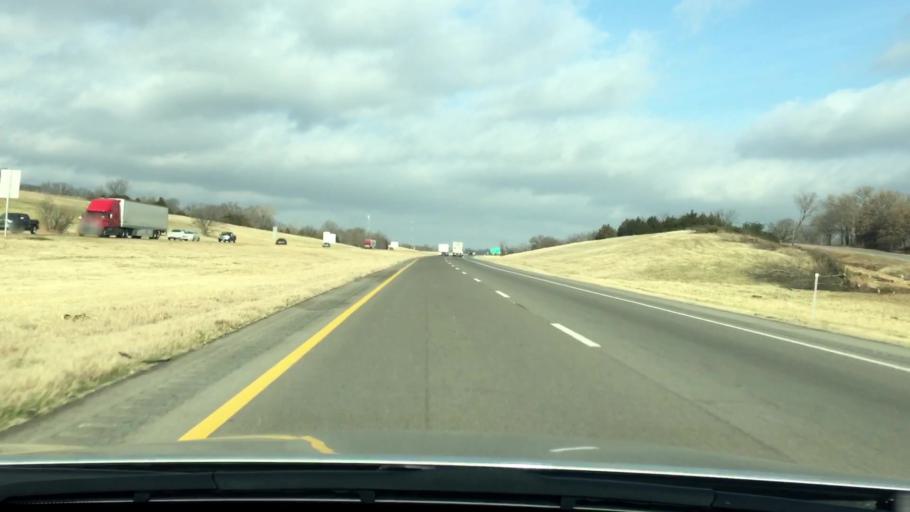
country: US
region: Oklahoma
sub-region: Garvin County
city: Pauls Valley
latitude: 34.7511
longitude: -97.2748
